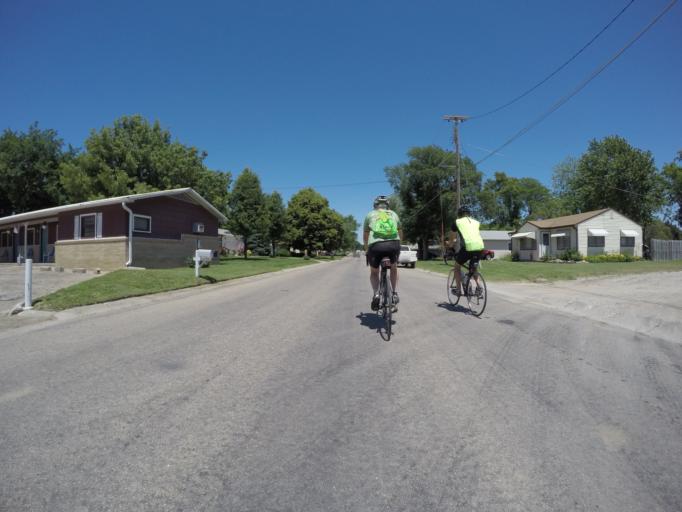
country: US
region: Kansas
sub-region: Republic County
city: Belleville
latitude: 39.8129
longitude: -97.6282
